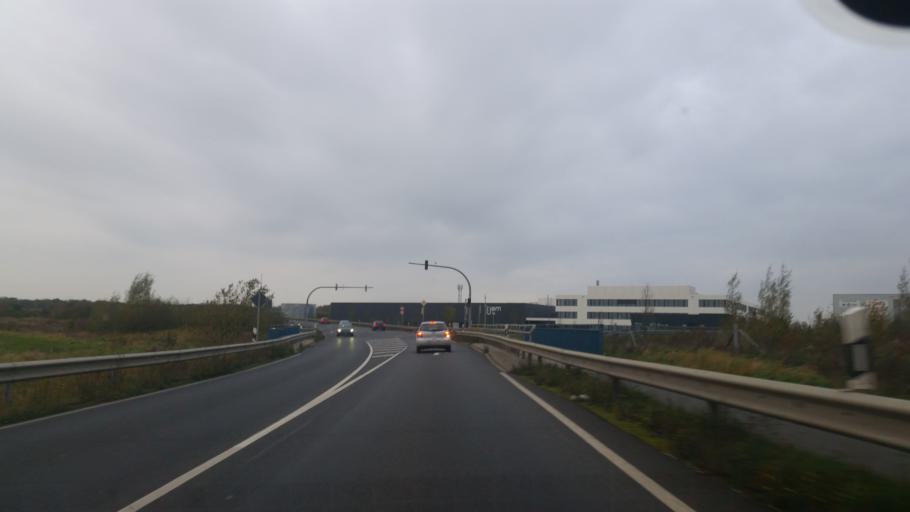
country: DE
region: Lower Saxony
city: Leiferde
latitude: 52.2073
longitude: 10.4953
